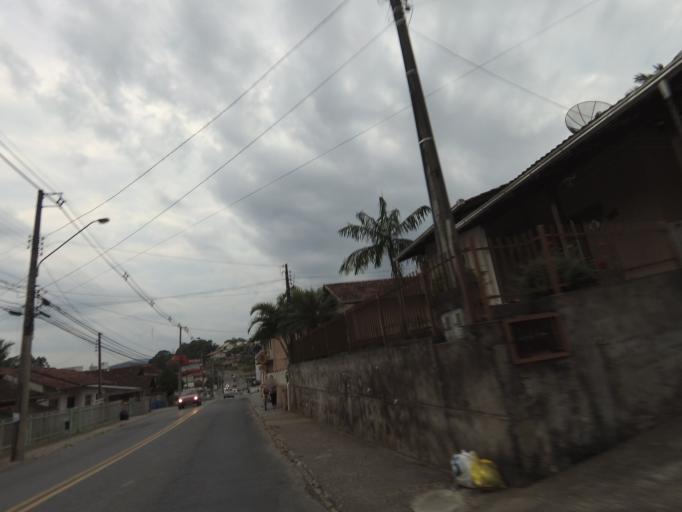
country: BR
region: Santa Catarina
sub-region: Blumenau
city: Blumenau
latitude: -26.8785
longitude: -49.0598
